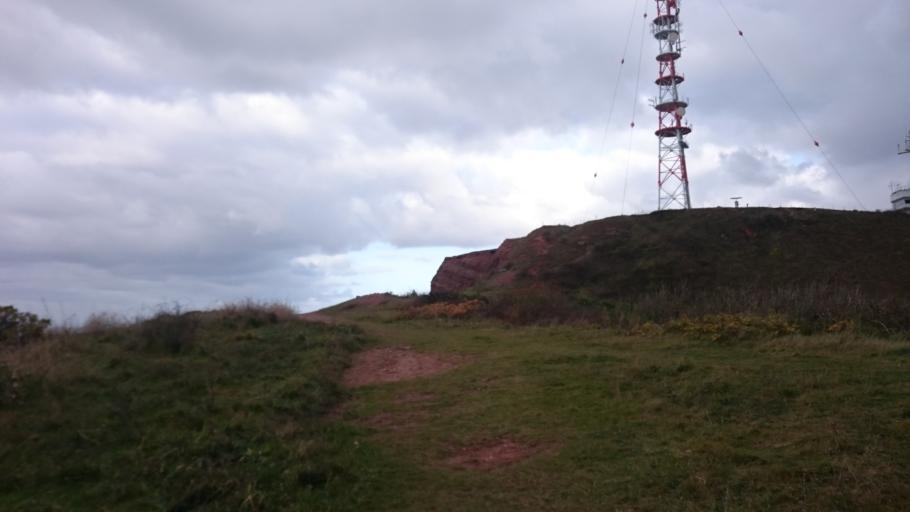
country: DE
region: Schleswig-Holstein
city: Helgoland
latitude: 54.1788
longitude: 7.8849
